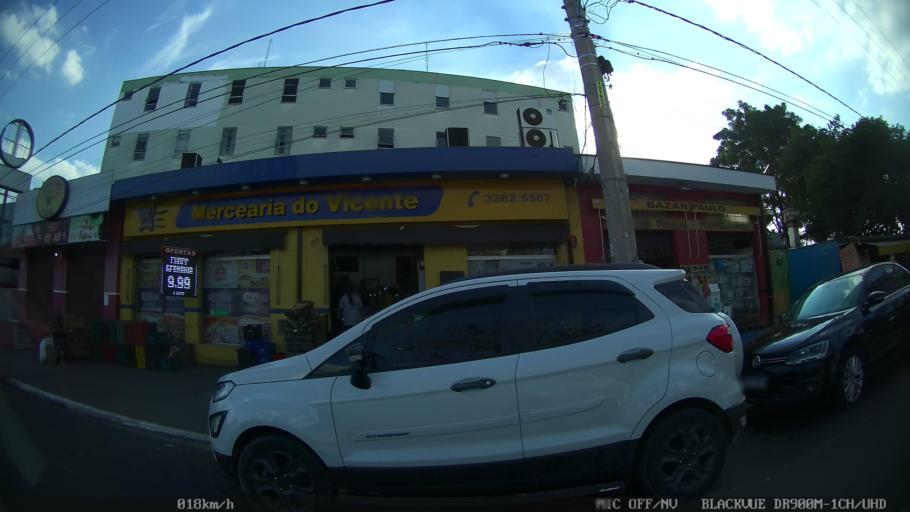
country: BR
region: Sao Paulo
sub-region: Hortolandia
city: Hortolandia
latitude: -22.8630
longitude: -47.1536
